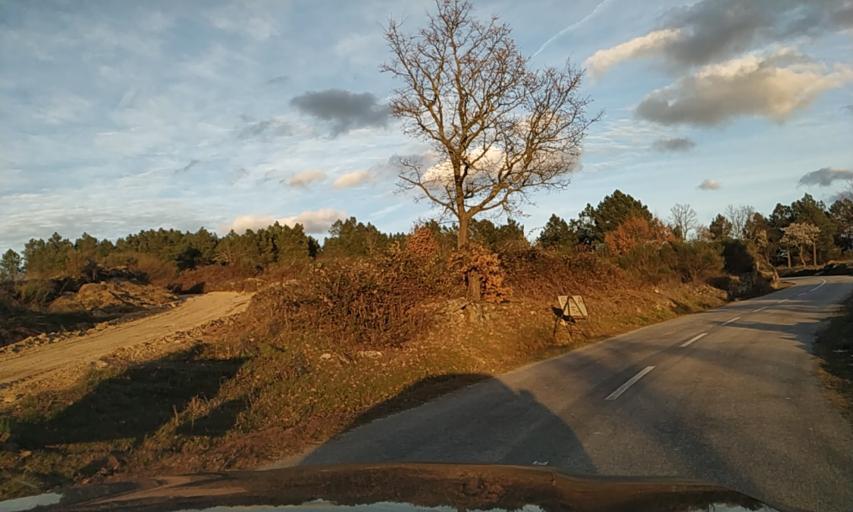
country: PT
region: Braganca
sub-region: Carrazeda de Ansiaes
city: Carrazeda de Anciaes
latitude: 41.2194
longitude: -7.3171
